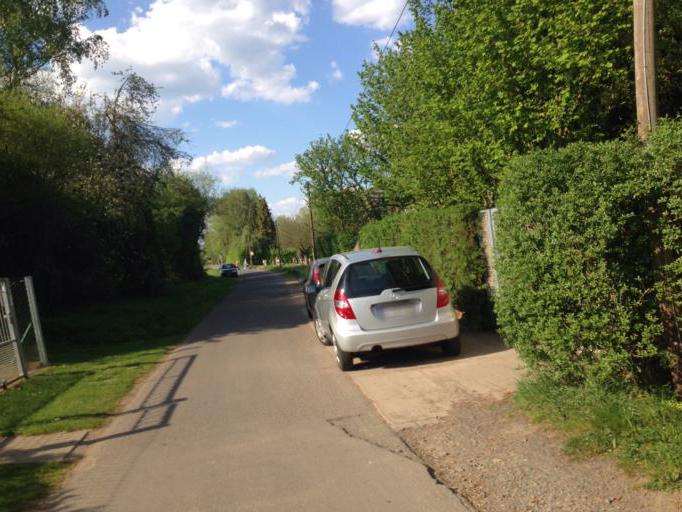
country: DE
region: Hesse
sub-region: Regierungsbezirk Giessen
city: Giessen
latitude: 50.6005
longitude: 8.6709
